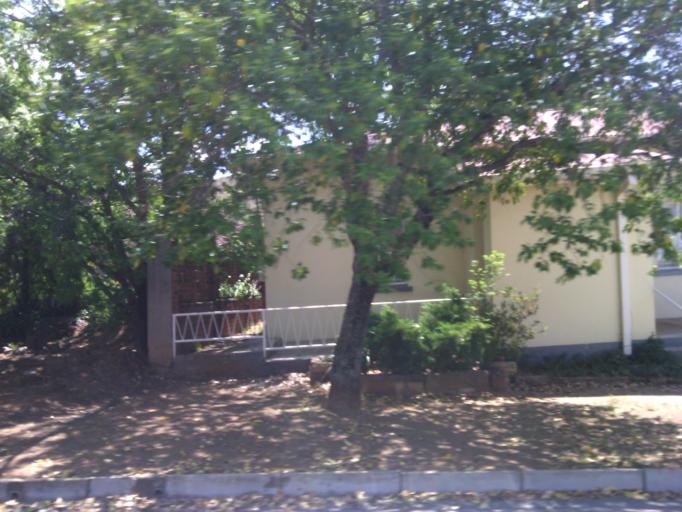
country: ZA
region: Orange Free State
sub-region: Xhariep District Municipality
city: Dewetsdorp
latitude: -29.5823
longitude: 26.6614
